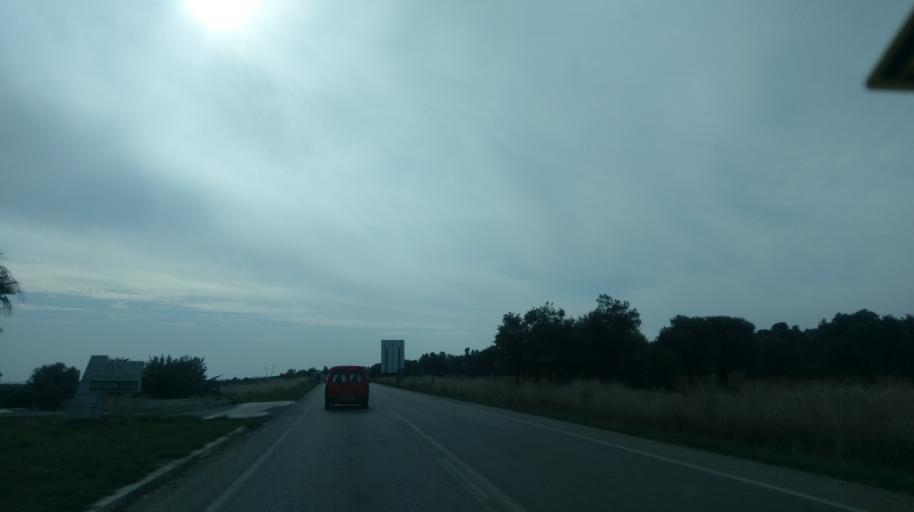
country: CY
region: Ammochostos
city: Leonarisso
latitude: 35.4172
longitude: 34.1208
